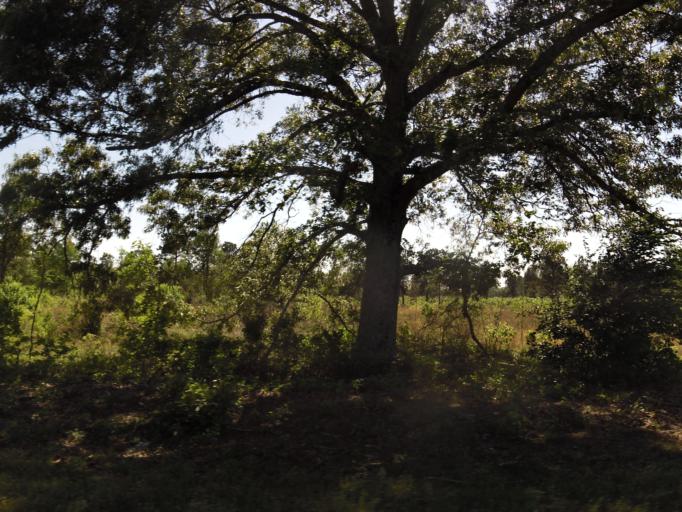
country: US
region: South Carolina
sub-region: Barnwell County
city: Williston
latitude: 33.4586
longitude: -81.4973
